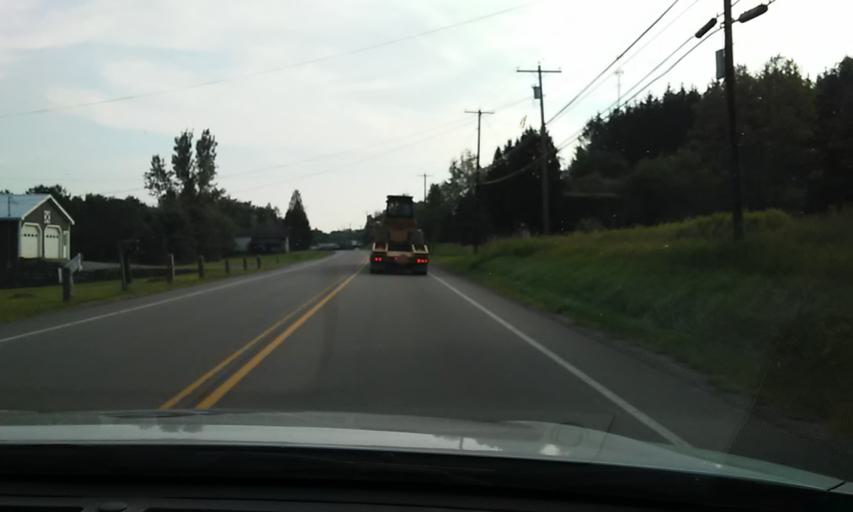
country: US
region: Pennsylvania
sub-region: McKean County
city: Kane
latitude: 41.7198
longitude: -78.6855
